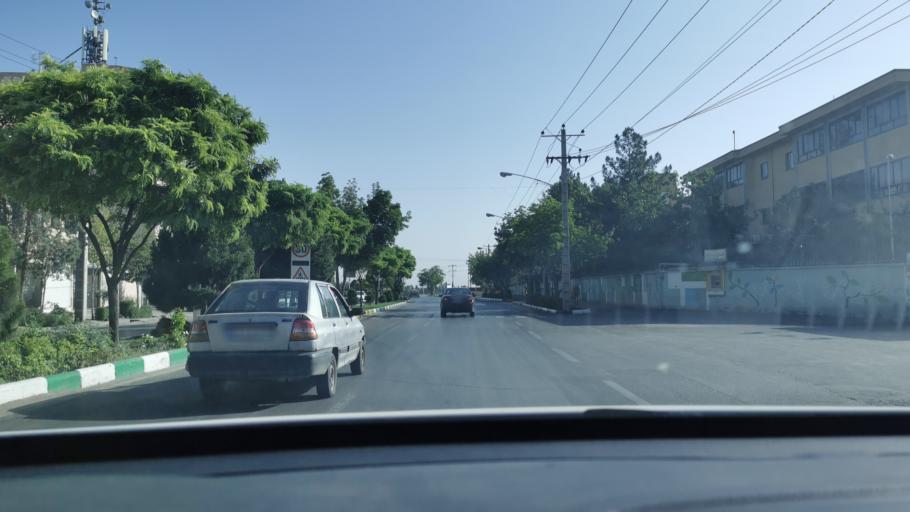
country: IR
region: Razavi Khorasan
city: Mashhad
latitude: 36.3390
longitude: 59.5071
